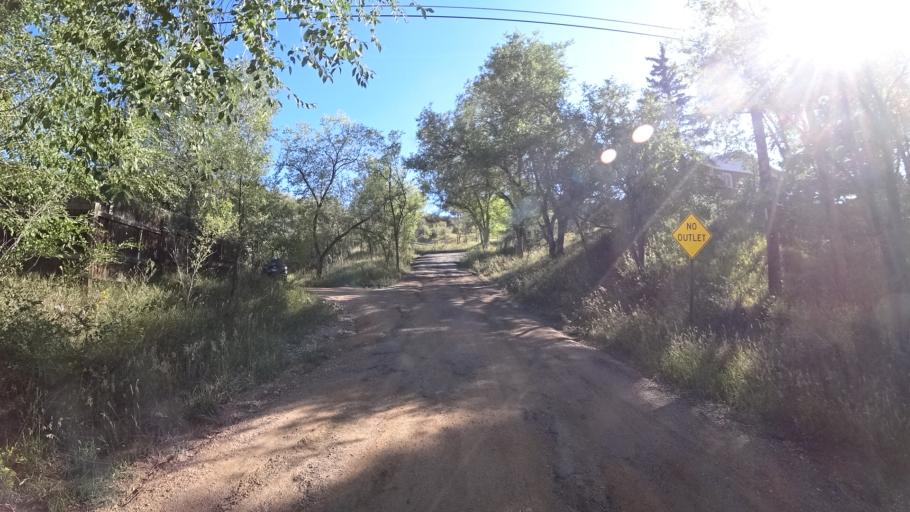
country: US
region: Colorado
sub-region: El Paso County
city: Colorado Springs
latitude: 38.8335
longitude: -104.8716
